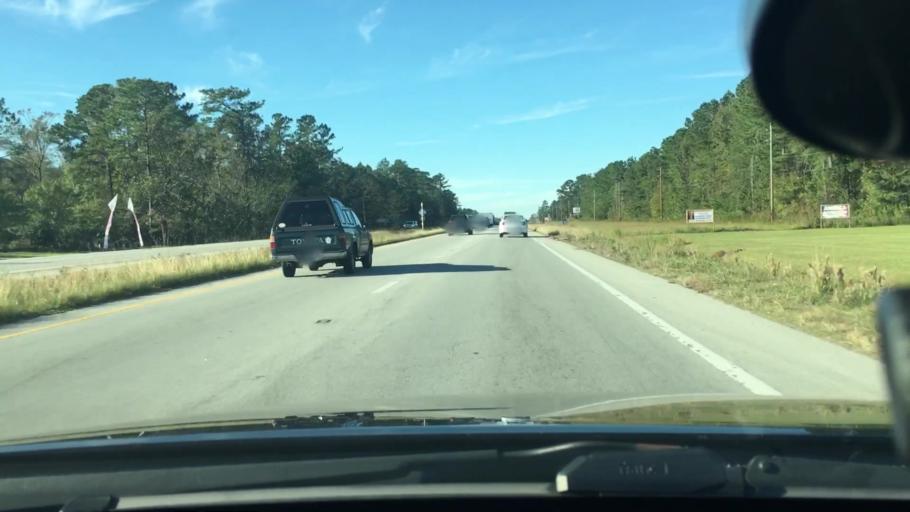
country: US
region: North Carolina
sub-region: Craven County
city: James City
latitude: 35.0507
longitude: -77.0145
